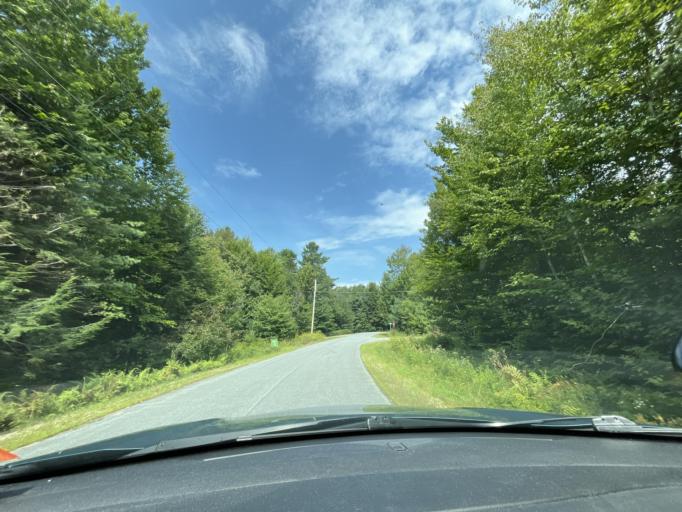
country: US
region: New Hampshire
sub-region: Merrimack County
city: New London
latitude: 43.4061
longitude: -71.9998
